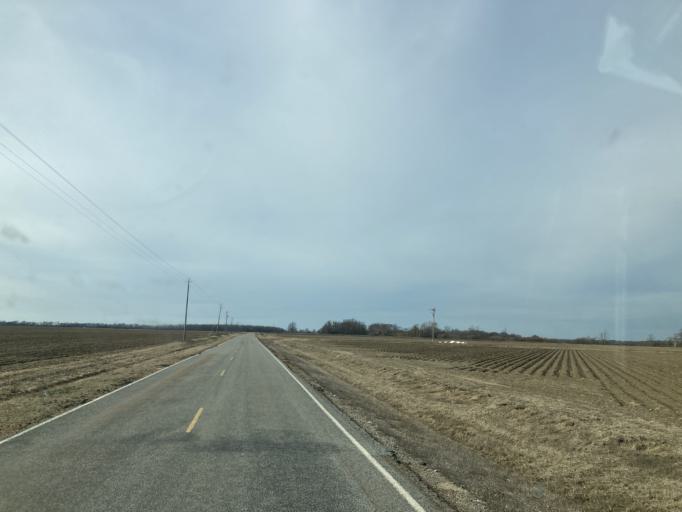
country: US
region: Mississippi
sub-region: Humphreys County
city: Belzoni
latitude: 33.0624
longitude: -90.6316
